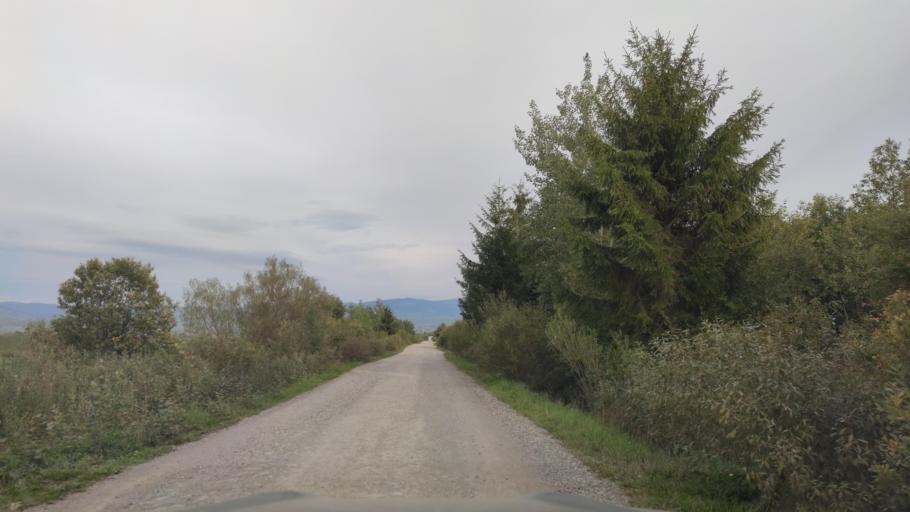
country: RO
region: Harghita
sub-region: Comuna Remetea
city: Remetea
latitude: 46.8120
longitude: 25.3751
